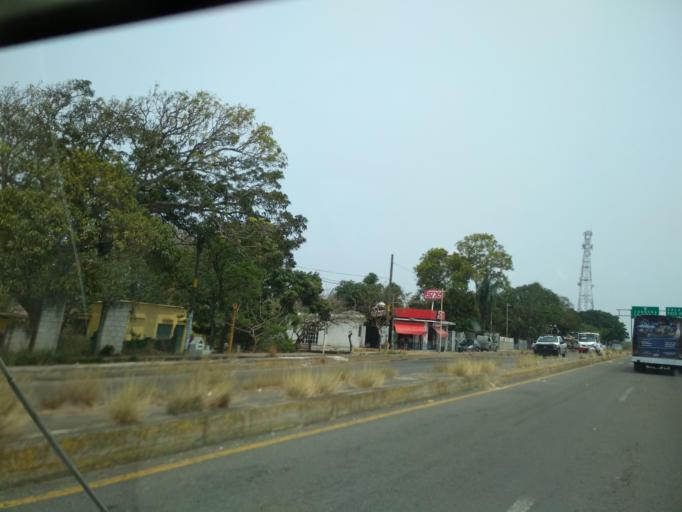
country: MX
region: Veracruz
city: Paso del Toro
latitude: 19.0314
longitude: -96.1378
